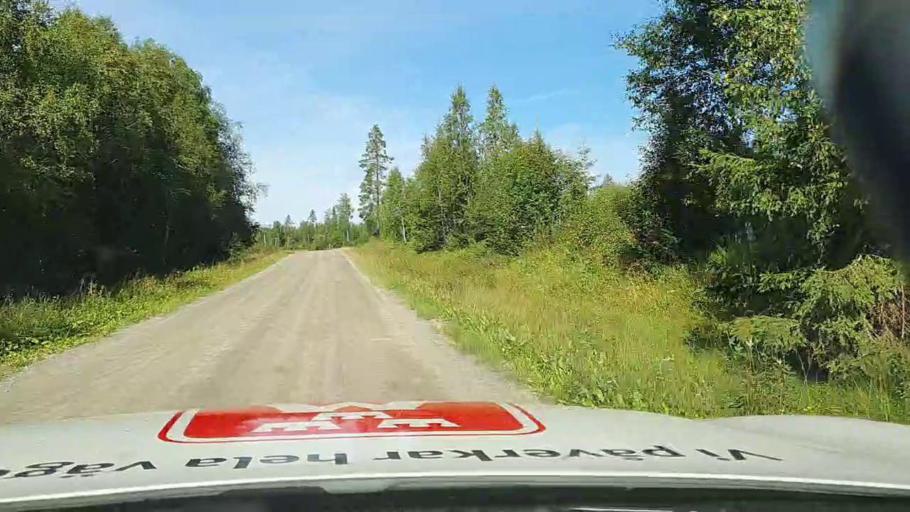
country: SE
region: Jaemtland
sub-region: Stroemsunds Kommun
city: Stroemsund
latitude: 63.7146
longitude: 15.2998
